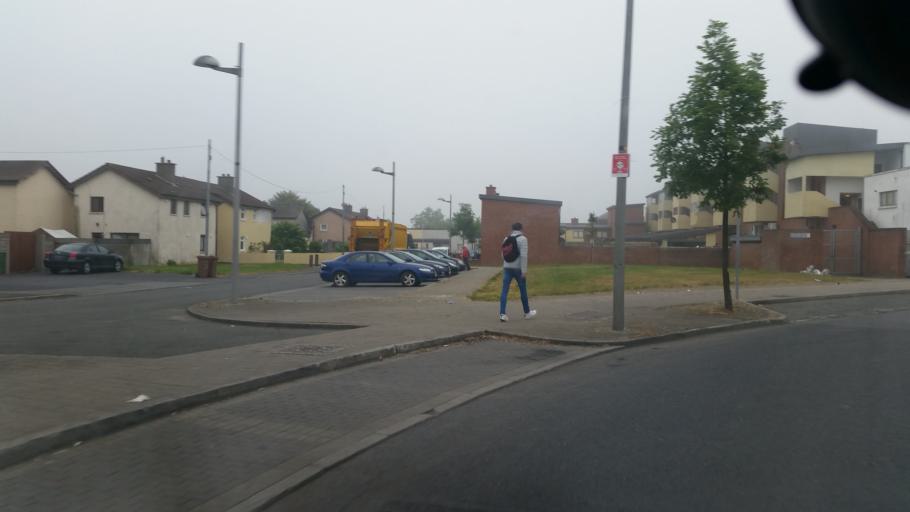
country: IE
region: Leinster
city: Ballymun
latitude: 53.4008
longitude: -6.2773
